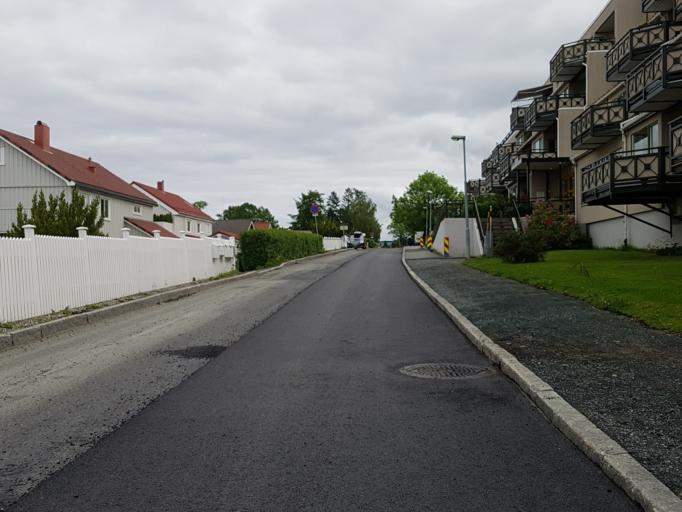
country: NO
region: Sor-Trondelag
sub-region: Trondheim
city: Trondheim
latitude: 63.4364
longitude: 10.4447
